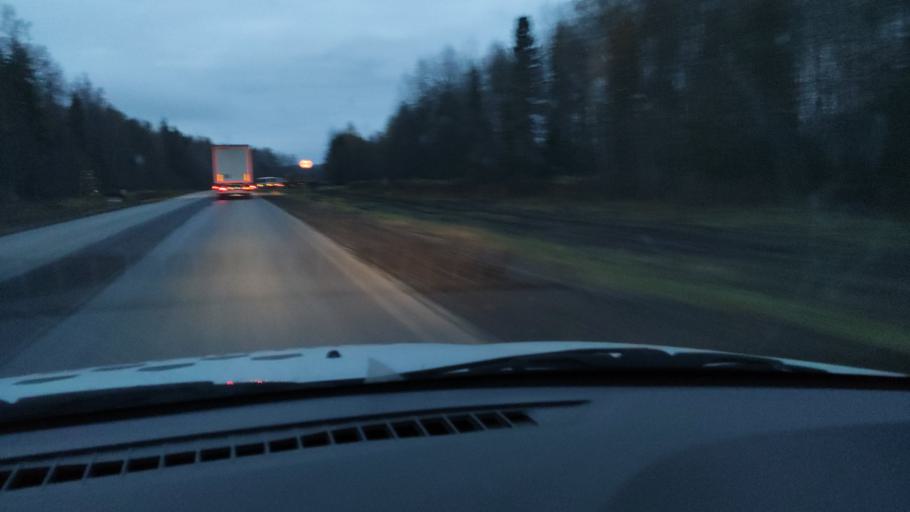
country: RU
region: Kirov
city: Kostino
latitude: 58.8280
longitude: 53.3833
